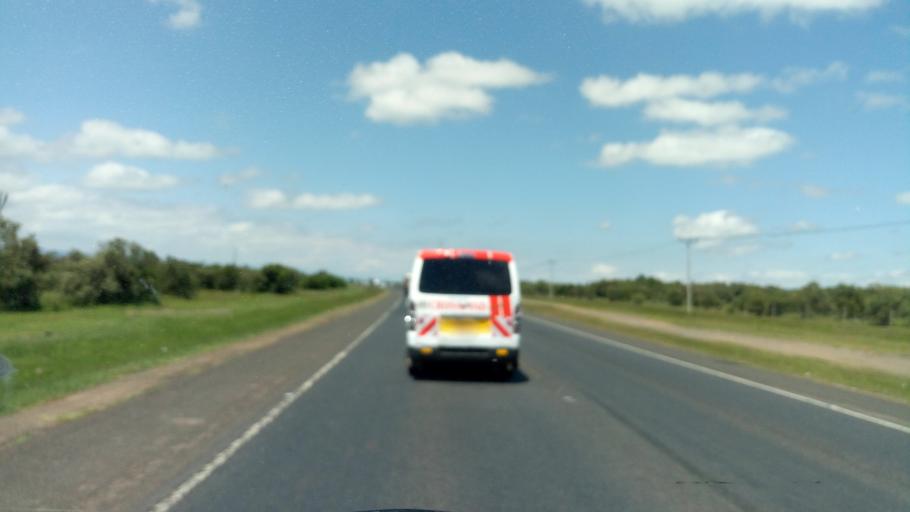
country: KE
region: Nakuru
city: Naivasha
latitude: -0.5336
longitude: 36.3335
